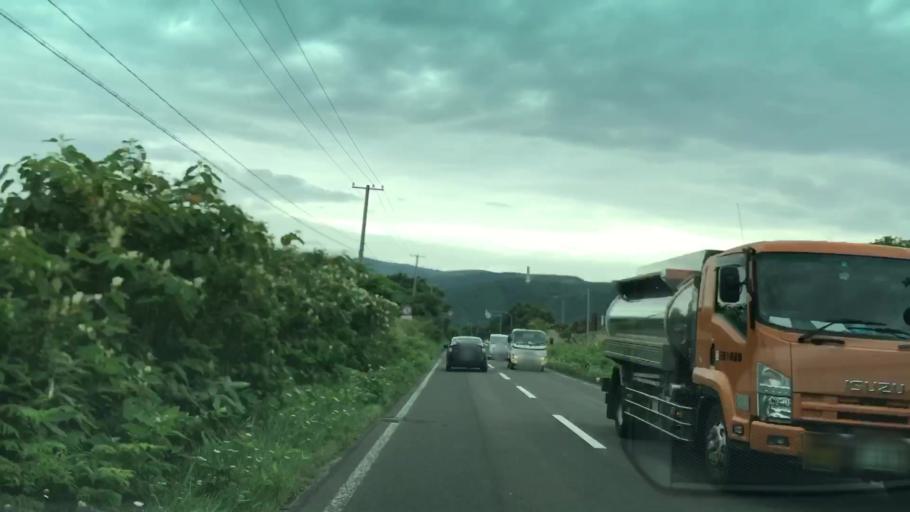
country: JP
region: Hokkaido
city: Iwanai
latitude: 42.8853
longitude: 140.3734
